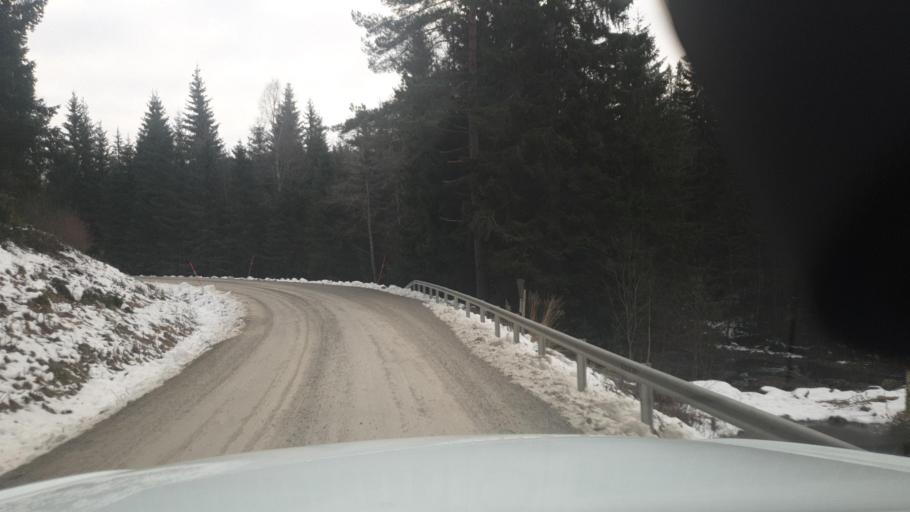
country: SE
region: Vaermland
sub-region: Sunne Kommun
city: Sunne
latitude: 59.8528
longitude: 12.9077
